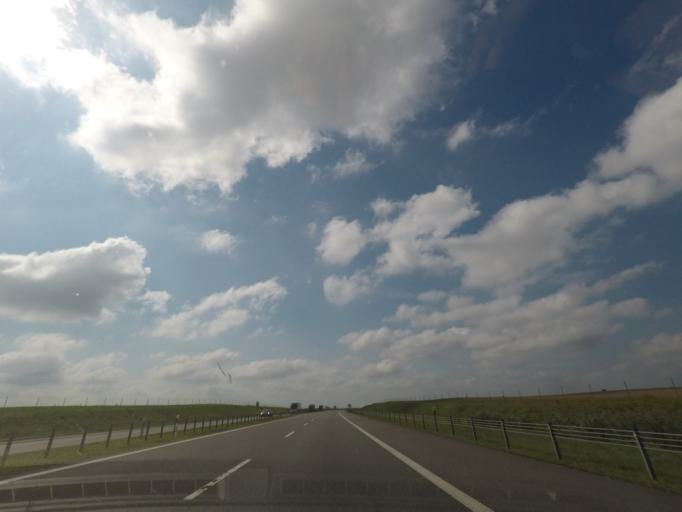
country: PL
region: Kujawsko-Pomorskie
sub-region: Powiat wabrzeski
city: Pluznica
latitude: 53.2035
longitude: 18.7403
